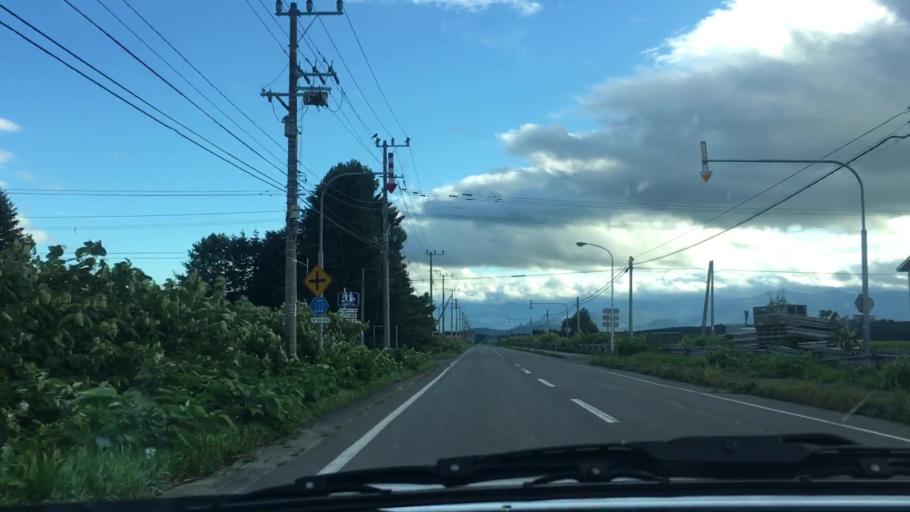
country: JP
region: Hokkaido
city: Otofuke
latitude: 43.1540
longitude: 142.9015
